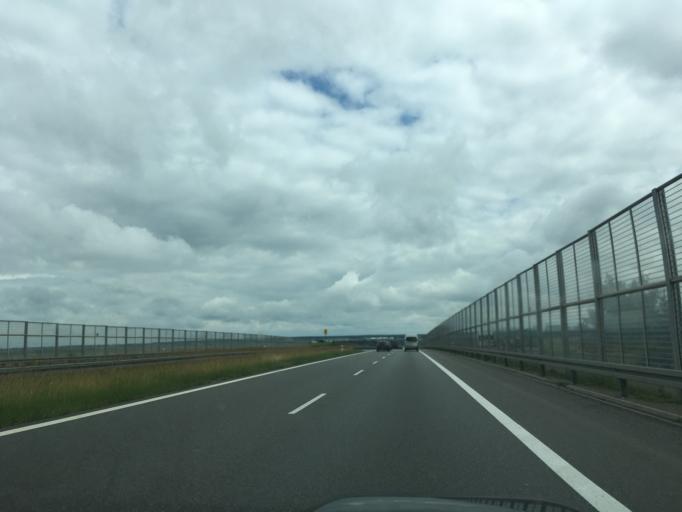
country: PL
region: Lublin Voivodeship
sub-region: Powiat lubelski
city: Jakubowice Murowane
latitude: 51.2863
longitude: 22.6240
